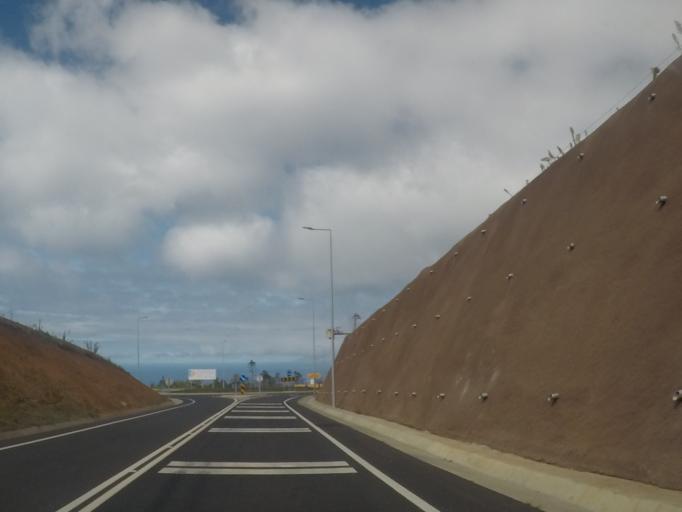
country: PT
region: Madeira
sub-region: Calheta
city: Faja da Ovelha
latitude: 32.8015
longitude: -17.2361
